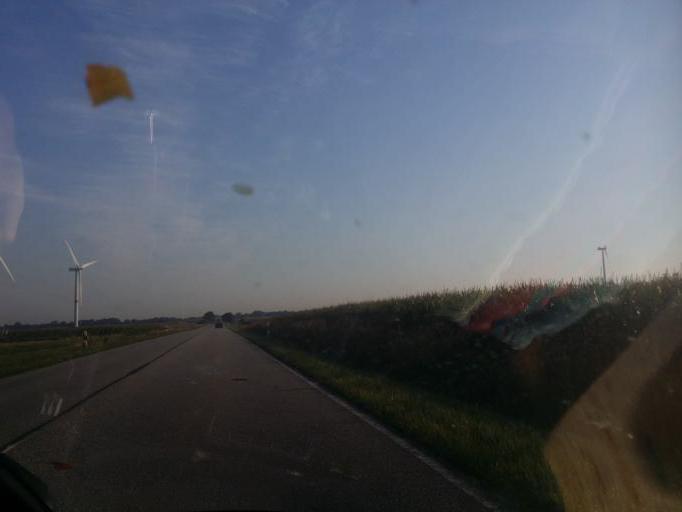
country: DE
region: Schleswig-Holstein
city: Braderup
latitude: 54.8172
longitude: 8.8861
